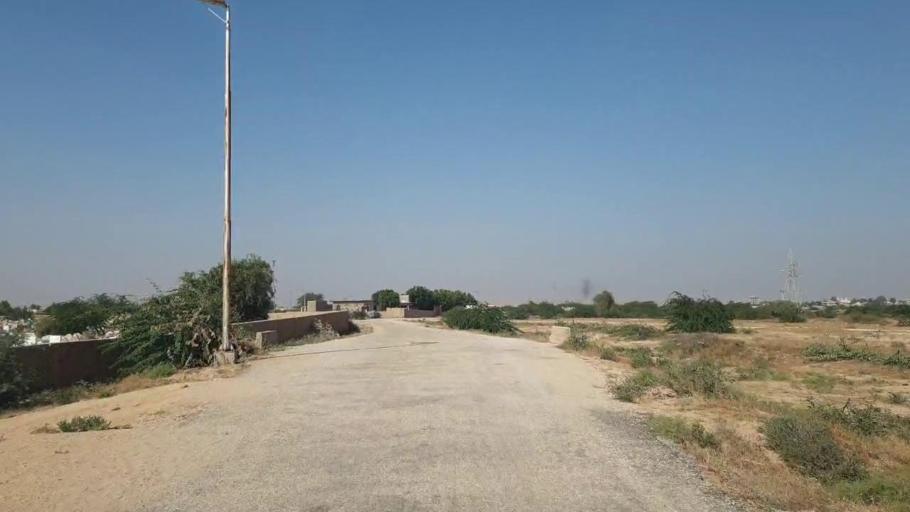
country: PK
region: Sindh
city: Jamshoro
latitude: 25.3511
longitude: 67.8320
